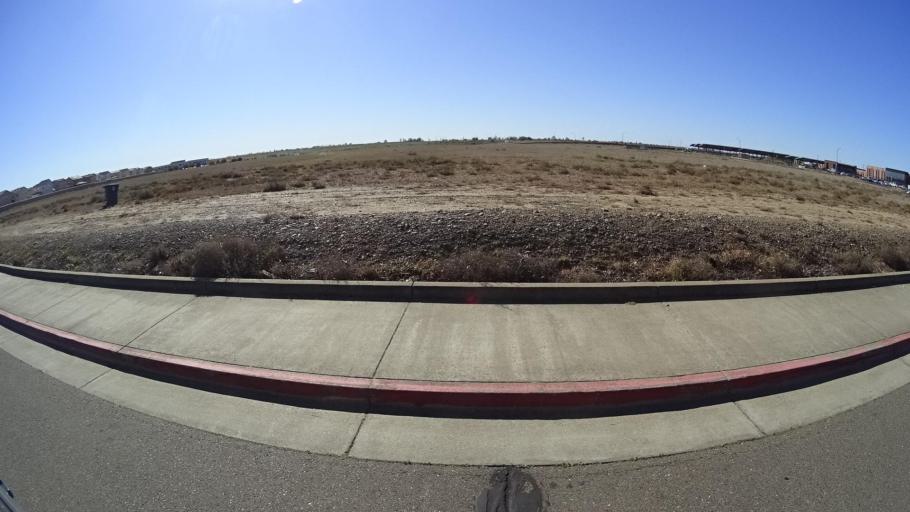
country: US
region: California
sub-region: Sacramento County
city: Rancho Cordova
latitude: 38.5717
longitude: -121.2836
